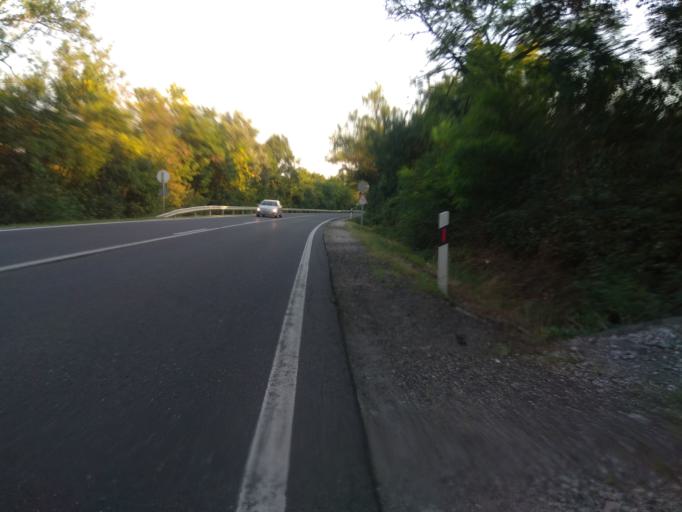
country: HU
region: Borsod-Abauj-Zemplen
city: Nyekladhaza
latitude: 47.9598
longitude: 20.8346
